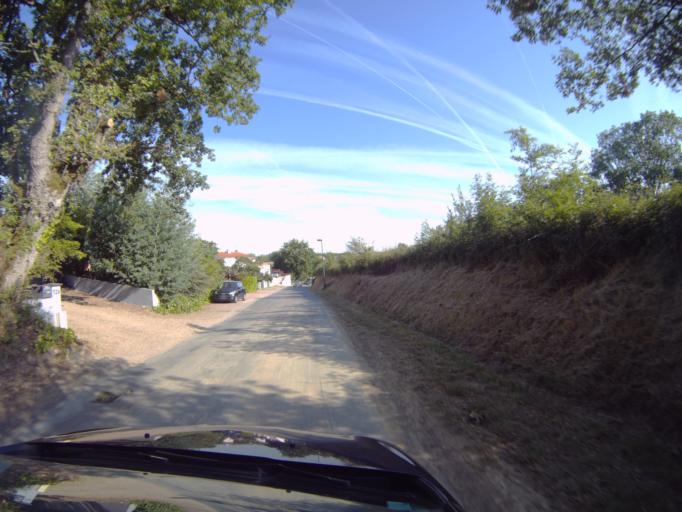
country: FR
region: Pays de la Loire
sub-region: Departement de la Vendee
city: Saint-Hilaire-de-Talmont
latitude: 46.4668
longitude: -1.6046
